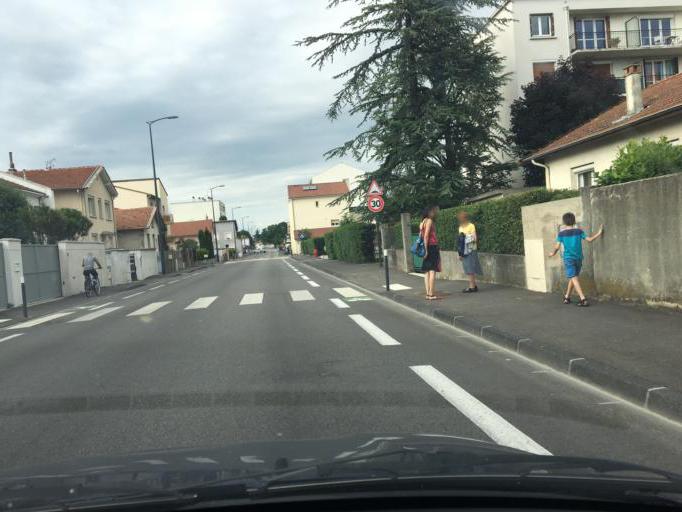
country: FR
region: Rhone-Alpes
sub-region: Departement de l'Ardeche
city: Guilherand-Granges
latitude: 44.9091
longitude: 4.8870
